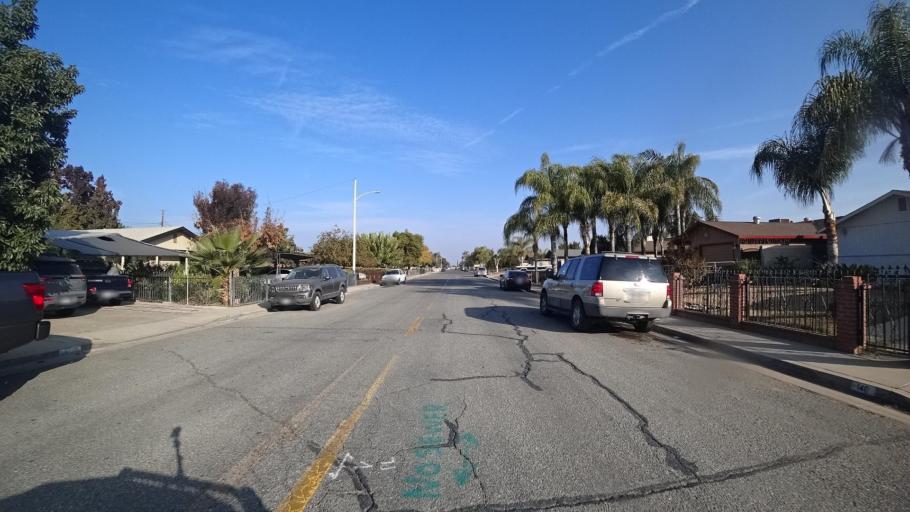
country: US
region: California
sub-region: Kern County
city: McFarland
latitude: 35.6751
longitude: -119.2185
